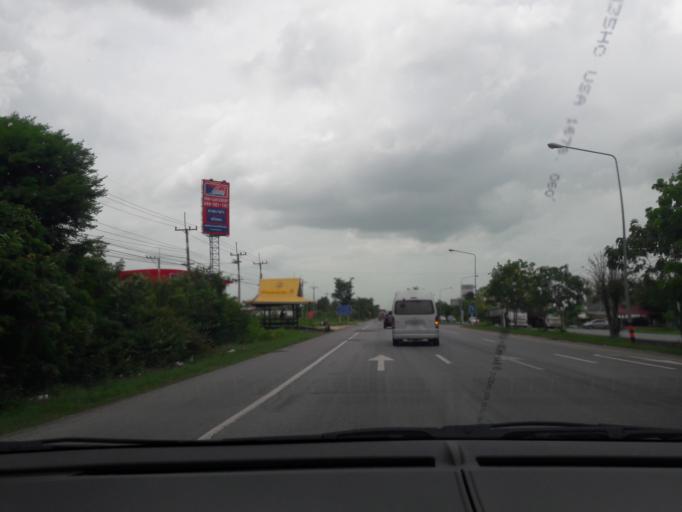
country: TH
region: Nakhon Ratchasima
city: Non Sung
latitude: 15.0948
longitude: 102.2513
